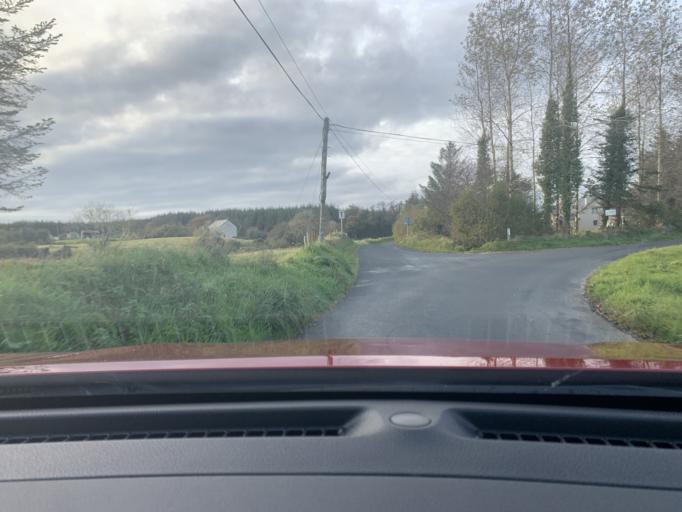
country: IE
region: Connaught
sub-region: Roscommon
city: Ballaghaderreen
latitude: 53.9174
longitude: -8.5920
